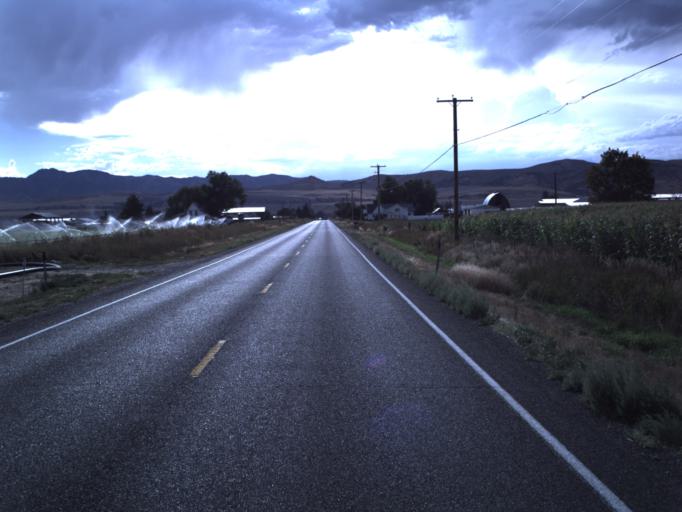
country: US
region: Utah
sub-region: Cache County
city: Lewiston
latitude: 41.9755
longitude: -111.9048
